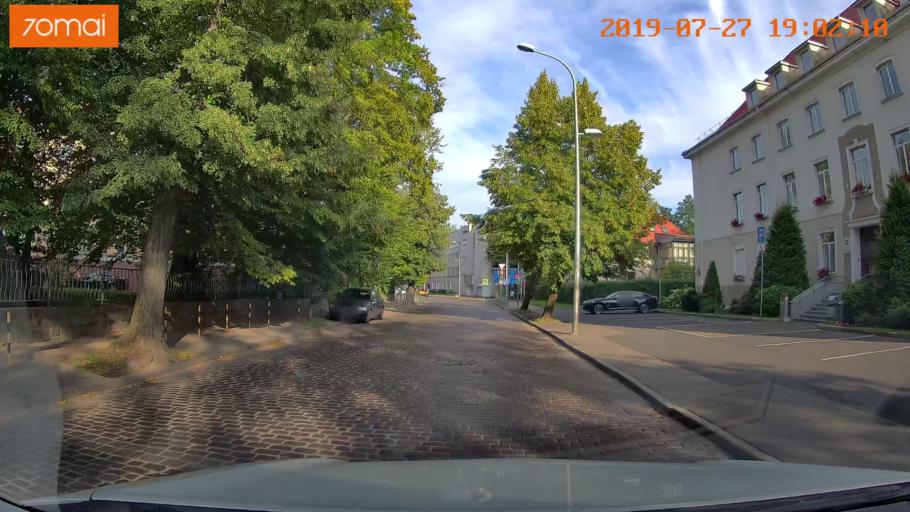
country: RU
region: Kaliningrad
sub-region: Gorod Kaliningrad
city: Kaliningrad
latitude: 54.7250
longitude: 20.4929
